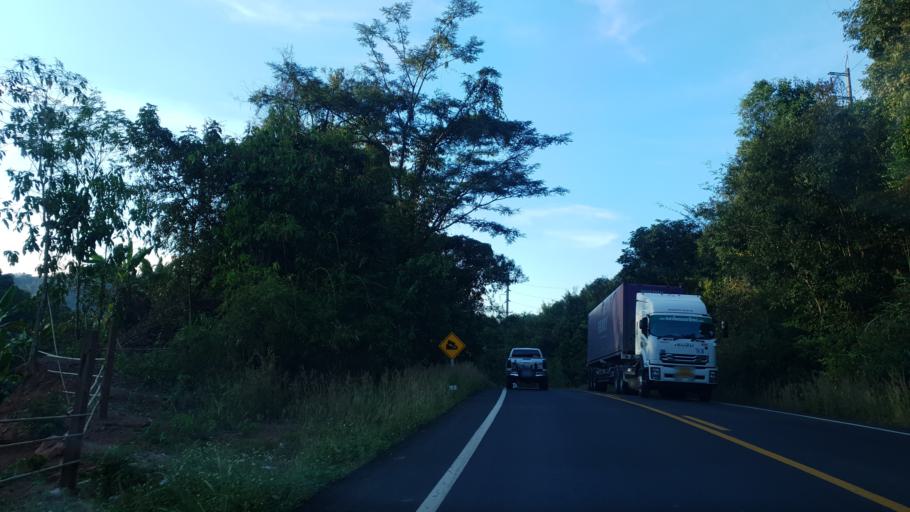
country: TH
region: Loei
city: Dan Sai
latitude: 17.2286
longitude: 101.0581
